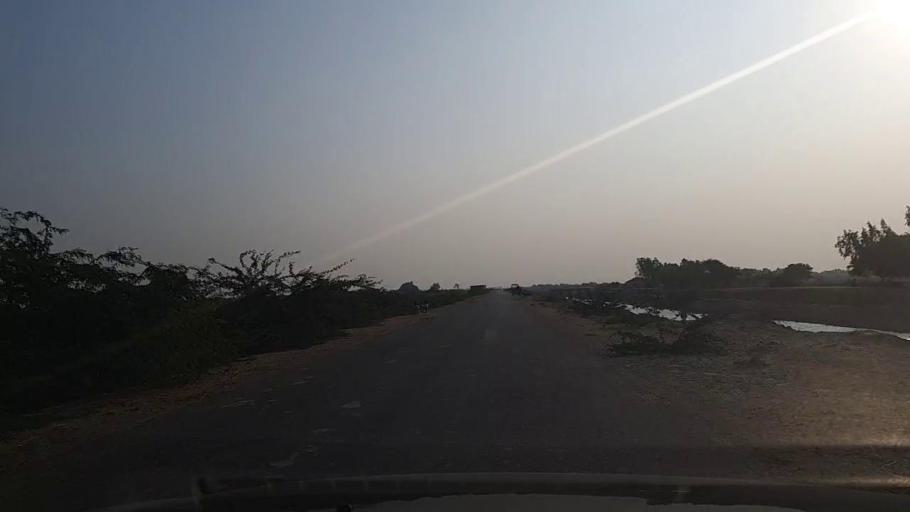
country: PK
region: Sindh
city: Mirpur Sakro
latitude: 24.4900
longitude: 67.8090
